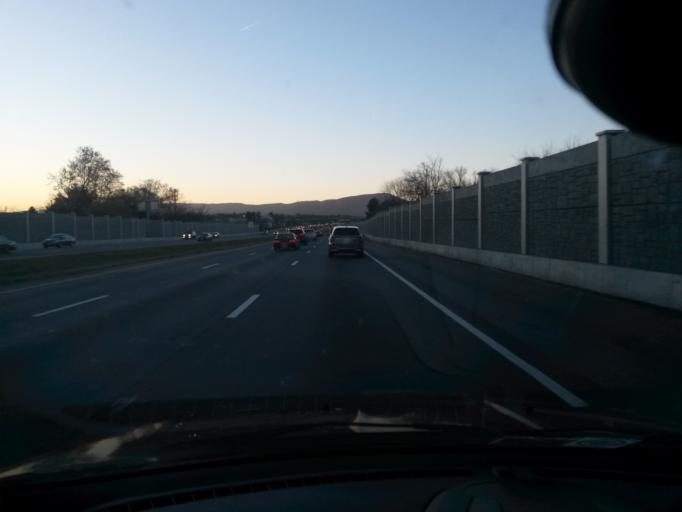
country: US
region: Virginia
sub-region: City of Roanoke
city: Roanoke
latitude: 37.2942
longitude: -79.9501
